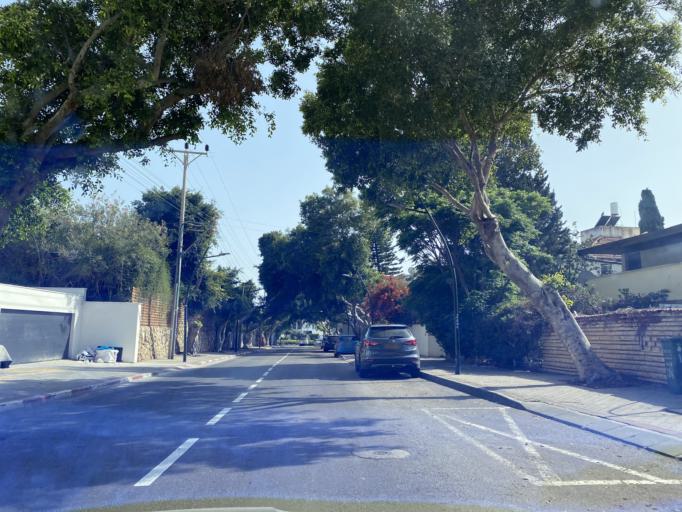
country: IL
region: Tel Aviv
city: Herzliya Pituah
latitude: 32.1693
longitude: 34.8063
